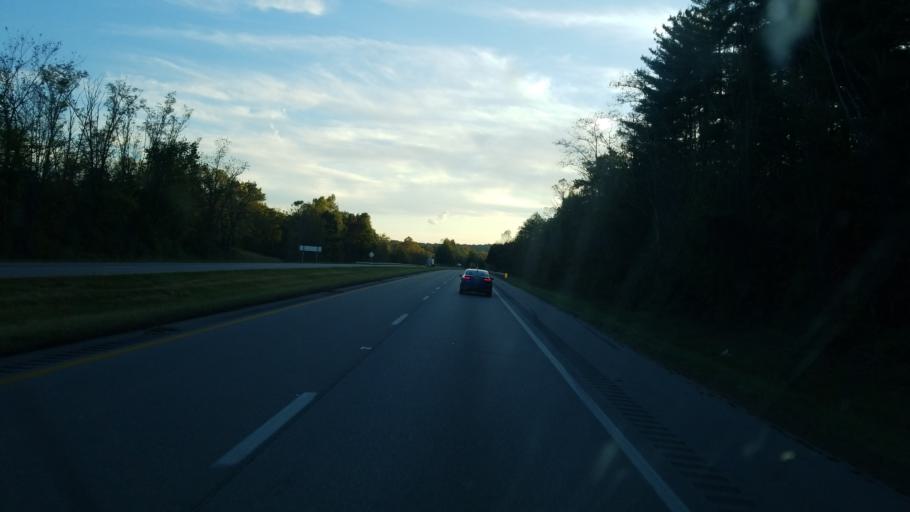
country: US
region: West Virginia
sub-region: Wood County
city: Washington
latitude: 39.2526
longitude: -81.7114
